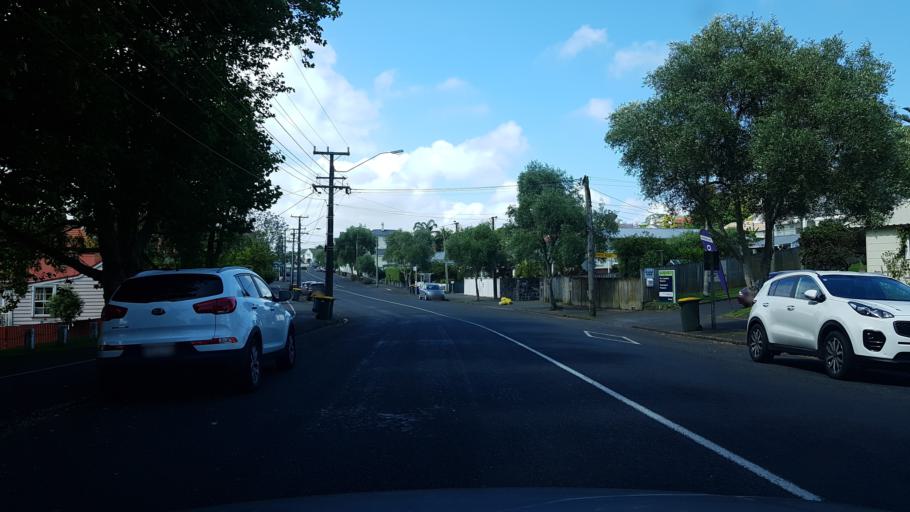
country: NZ
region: Auckland
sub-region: Auckland
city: Auckland
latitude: -36.8253
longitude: 174.8034
